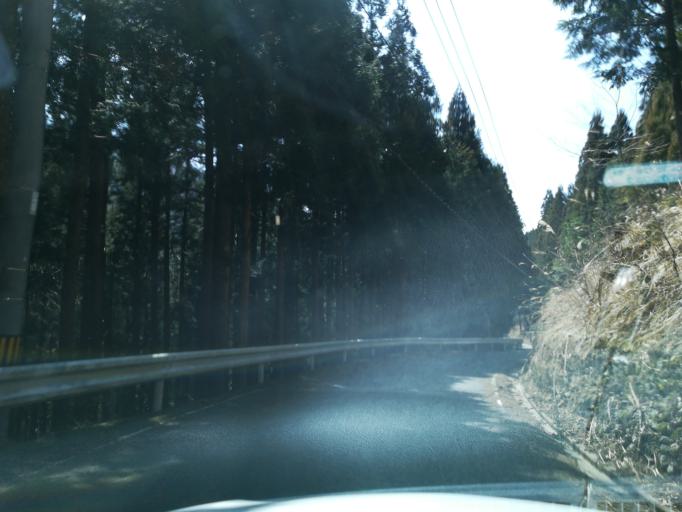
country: JP
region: Tokushima
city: Wakimachi
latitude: 33.8618
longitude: 134.0650
